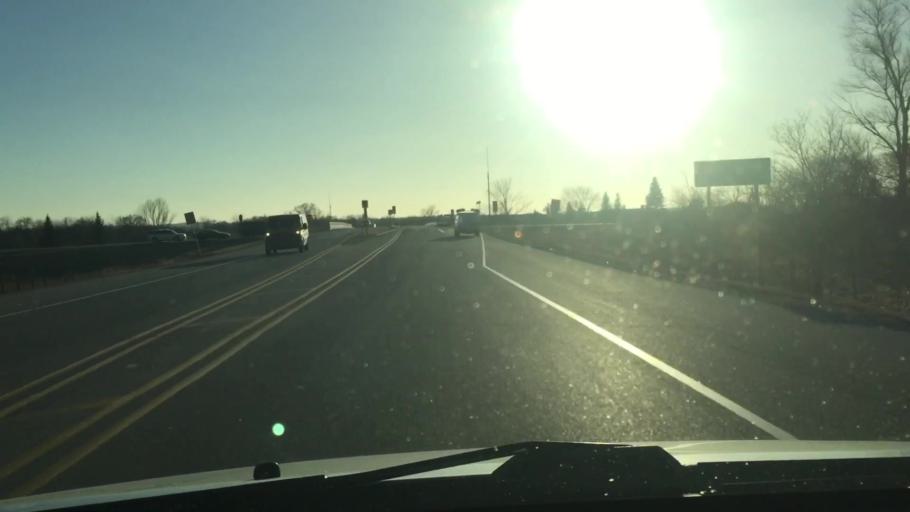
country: US
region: Wisconsin
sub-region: Waukesha County
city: Pewaukee
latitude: 43.0967
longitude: -88.2710
